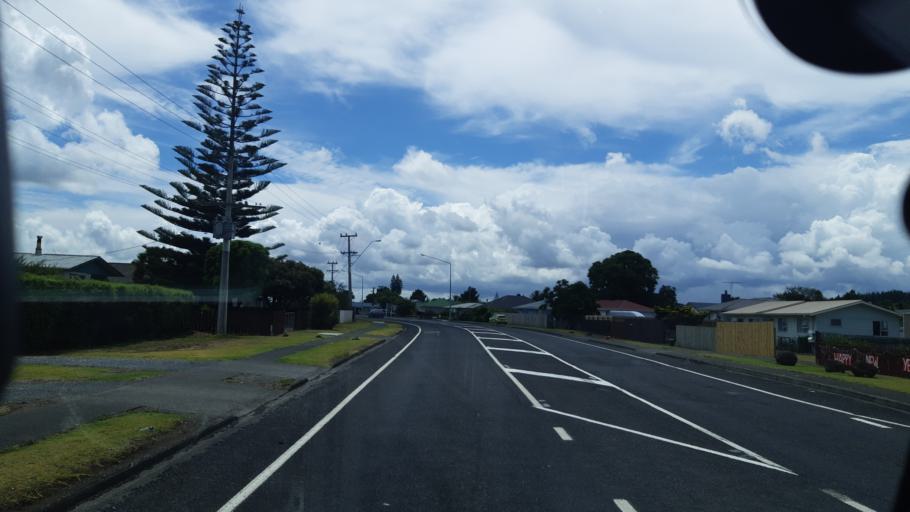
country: NZ
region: Northland
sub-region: Far North District
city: Moerewa
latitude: -35.3894
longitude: 174.0087
